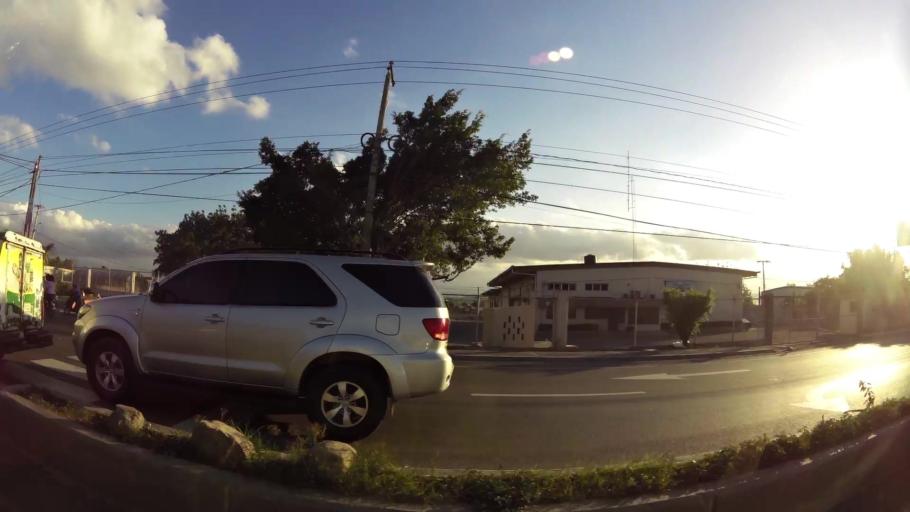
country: DO
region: Santiago
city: Palmar Arriba
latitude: 19.4922
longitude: -70.7270
